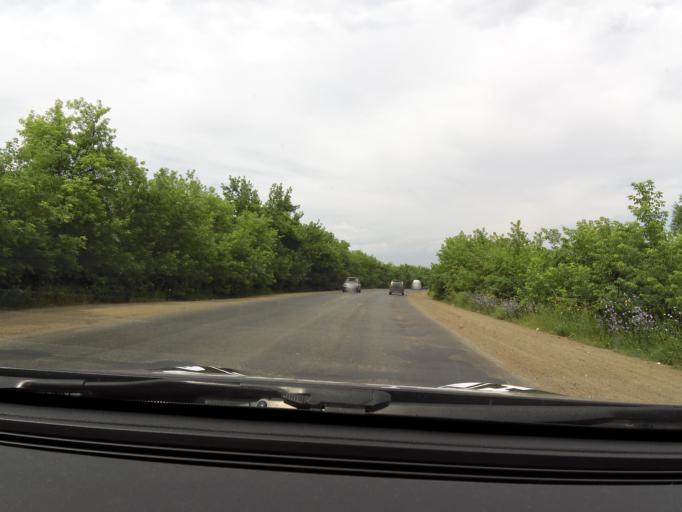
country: RU
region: Bashkortostan
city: Iglino
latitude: 54.7746
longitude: 56.2448
